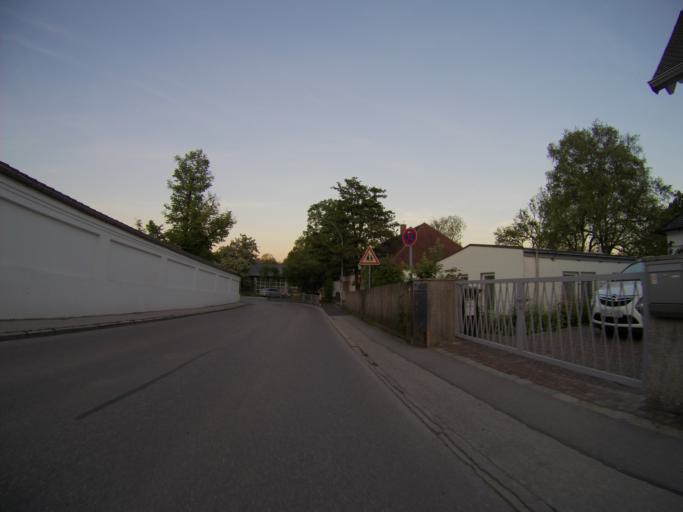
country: DE
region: Bavaria
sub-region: Upper Bavaria
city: Freising
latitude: 48.4079
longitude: 11.7553
